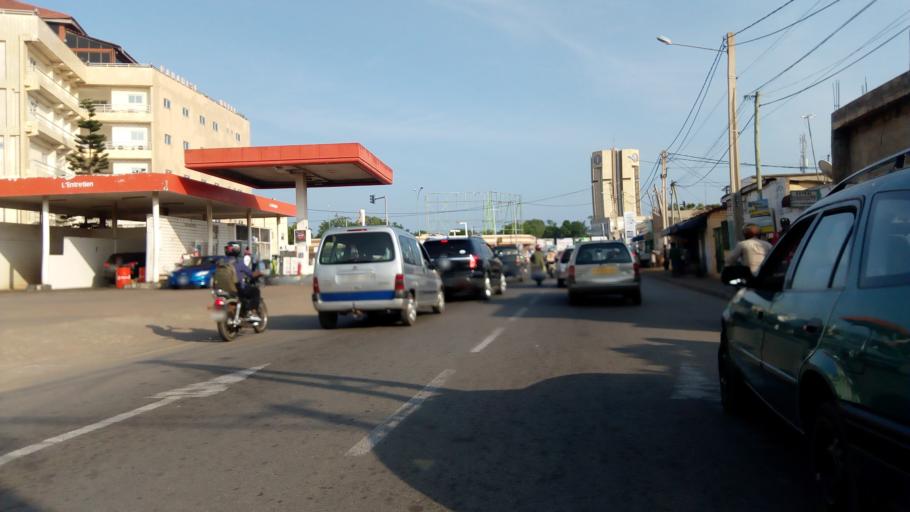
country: TG
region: Maritime
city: Lome
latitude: 6.1313
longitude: 1.2120
